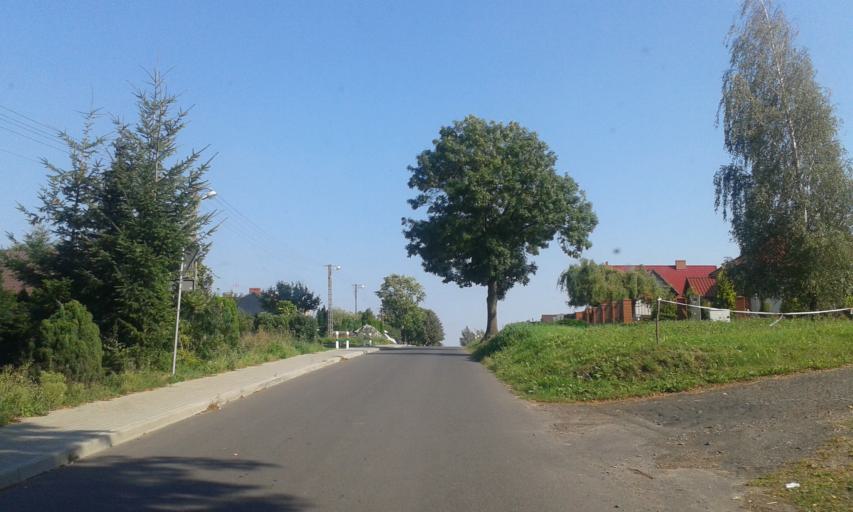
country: PL
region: Kujawsko-Pomorskie
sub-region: Powiat swiecki
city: Nowe
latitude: 53.6739
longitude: 18.7273
